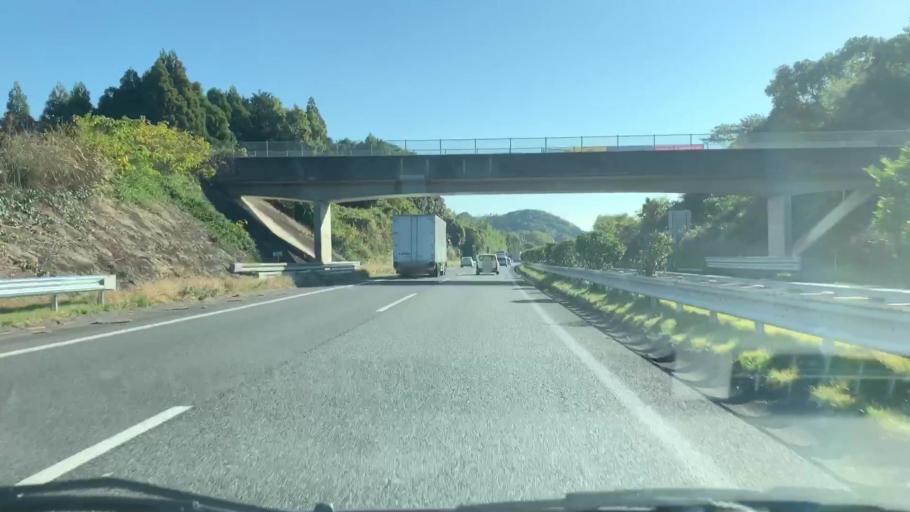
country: JP
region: Saga Prefecture
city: Saga-shi
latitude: 33.3109
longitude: 130.2160
